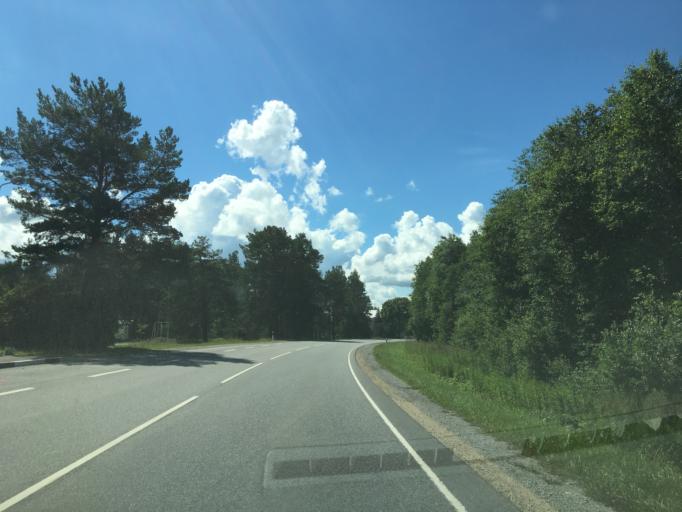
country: EE
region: Harju
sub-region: Nissi vald
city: Riisipere
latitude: 59.2392
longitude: 24.2756
